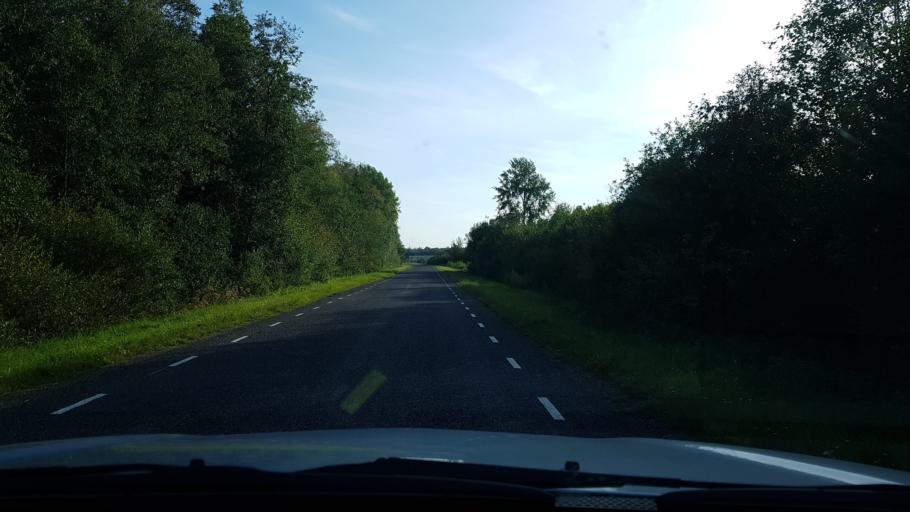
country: EE
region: Ida-Virumaa
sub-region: Narva-Joesuu linn
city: Narva-Joesuu
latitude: 59.3777
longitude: 28.0727
